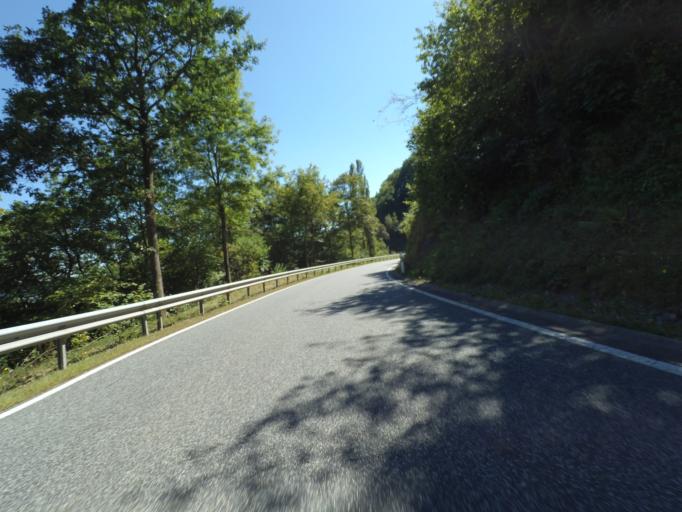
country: DE
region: Rheinland-Pfalz
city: Bremm
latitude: 50.0966
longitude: 7.1106
